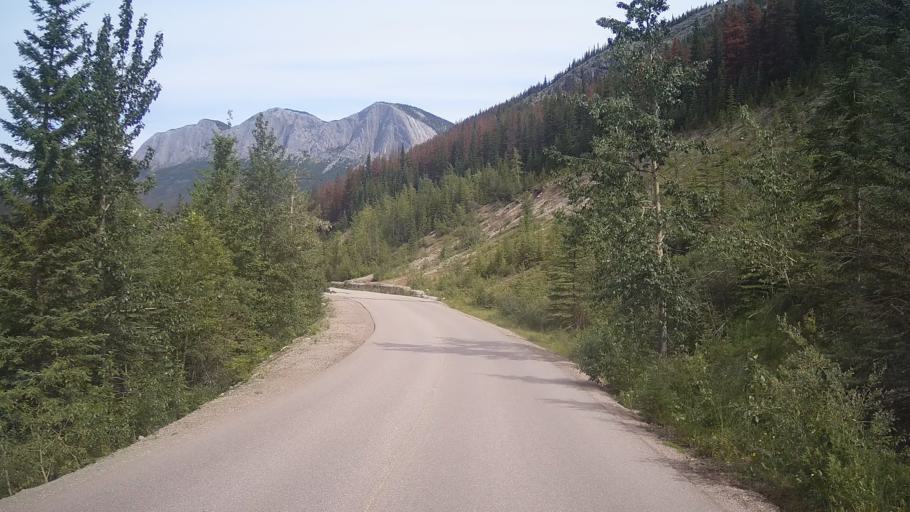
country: CA
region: Alberta
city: Hinton
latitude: 53.1335
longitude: -117.7717
